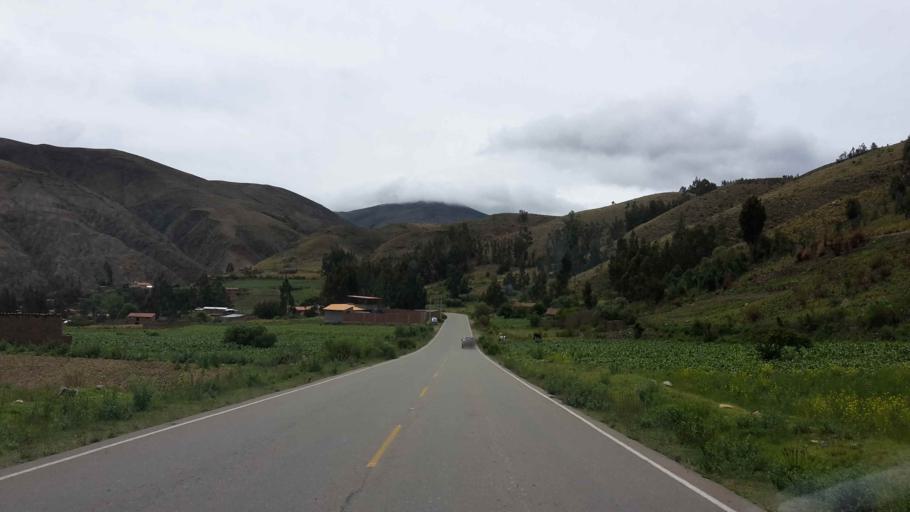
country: BO
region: Cochabamba
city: Colomi
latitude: -17.4103
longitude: -65.7762
